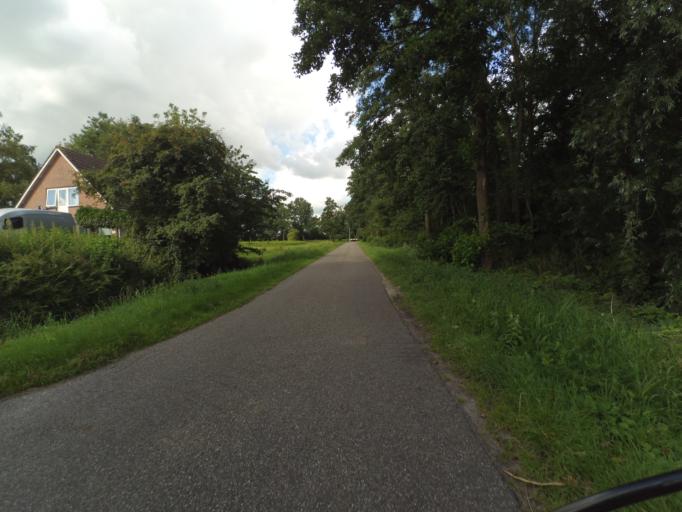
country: NL
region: Friesland
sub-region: Gemeente Tytsjerksteradiel
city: Tytsjerk
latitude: 53.2345
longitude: 5.9233
